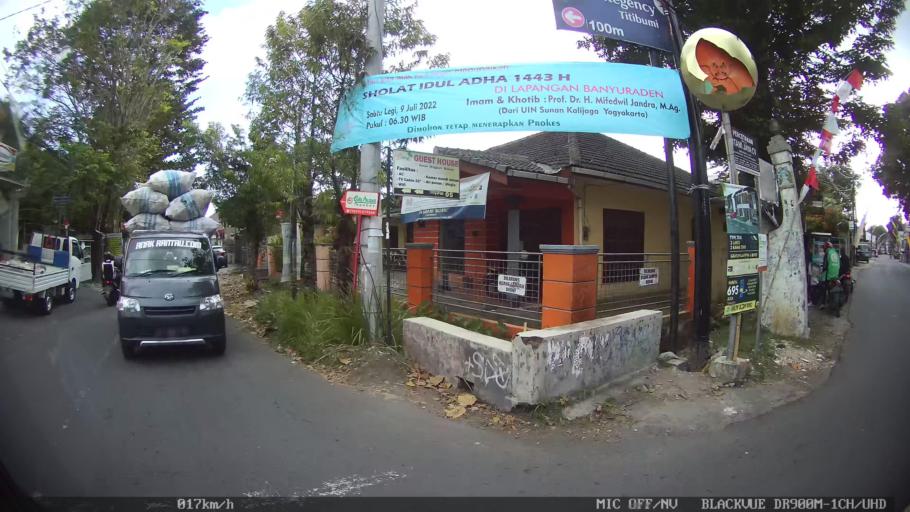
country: ID
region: Daerah Istimewa Yogyakarta
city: Yogyakarta
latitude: -7.7841
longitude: 110.3419
